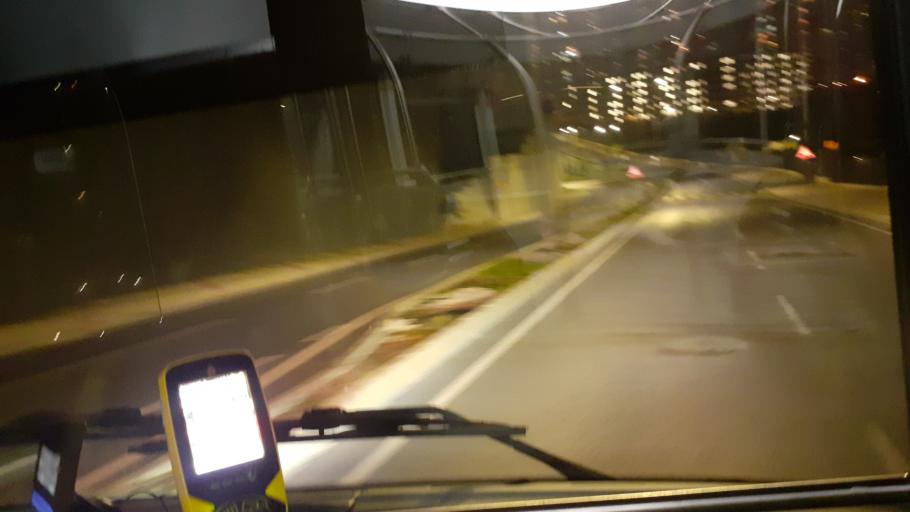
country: TR
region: Istanbul
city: Basaksehir
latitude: 41.0702
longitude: 28.7792
